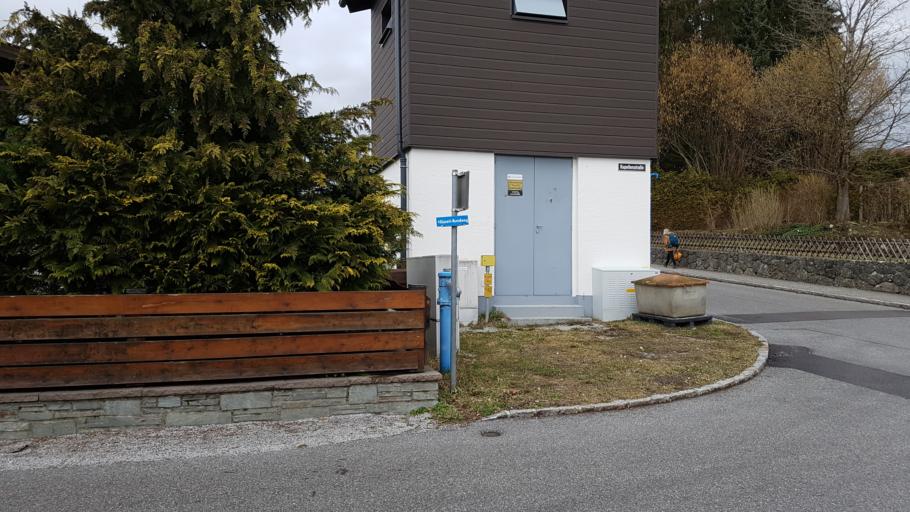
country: AT
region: Salzburg
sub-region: Politischer Bezirk Salzburg-Umgebung
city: Henndorf am Wallersee
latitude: 47.8989
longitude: 13.1830
